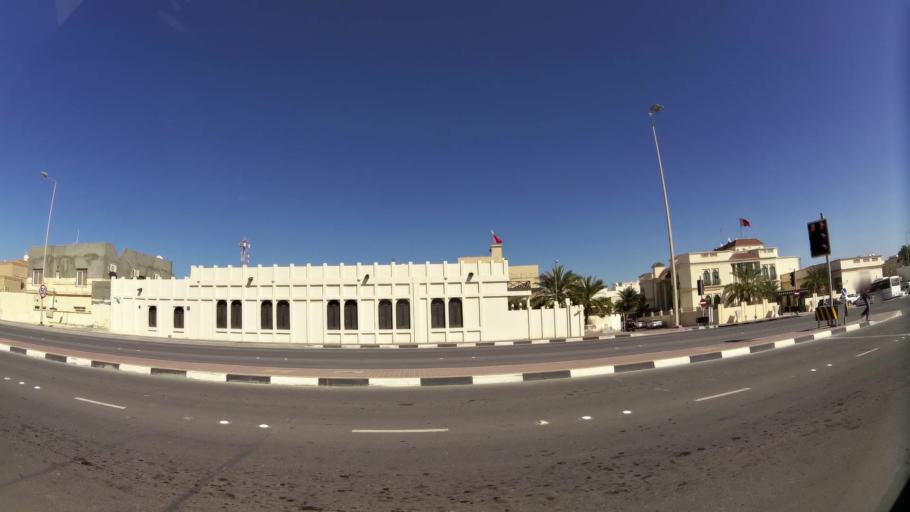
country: BH
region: Muharraq
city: Al Hadd
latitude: 26.2471
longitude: 50.6522
